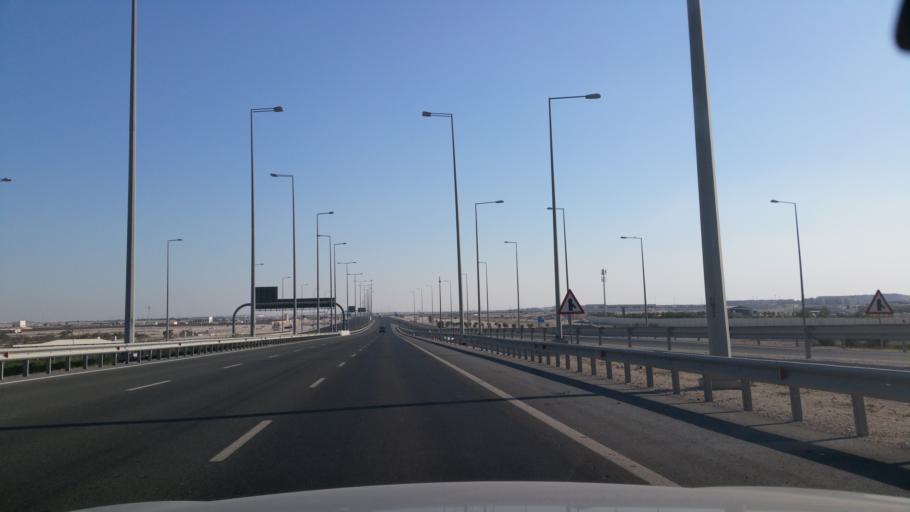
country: QA
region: Al Wakrah
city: Al Wukayr
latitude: 25.1624
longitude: 51.4727
